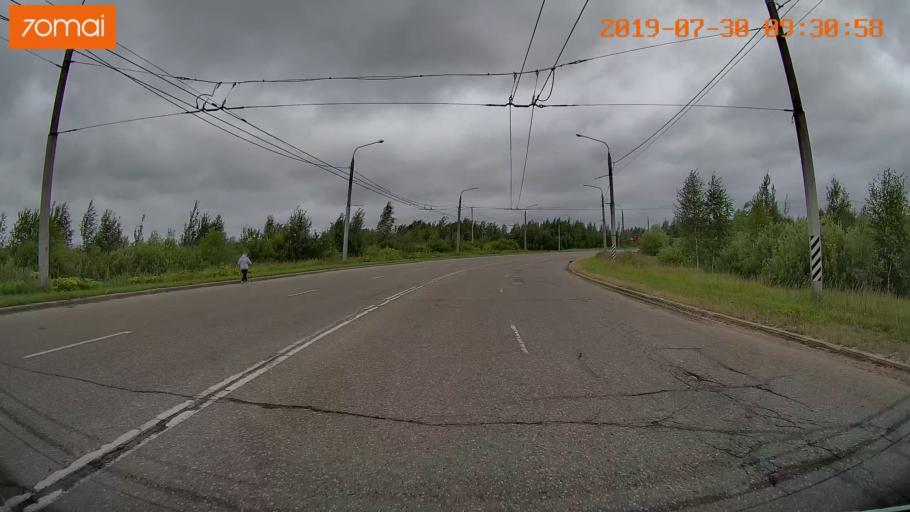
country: RU
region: Ivanovo
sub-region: Gorod Ivanovo
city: Ivanovo
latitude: 56.9510
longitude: 40.9476
